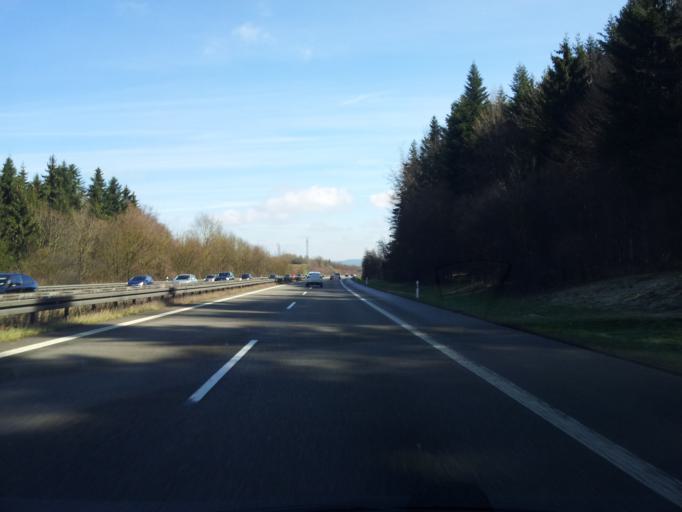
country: DE
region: Baden-Wuerttemberg
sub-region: Freiburg Region
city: Villingendorf
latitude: 48.1882
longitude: 8.5829
